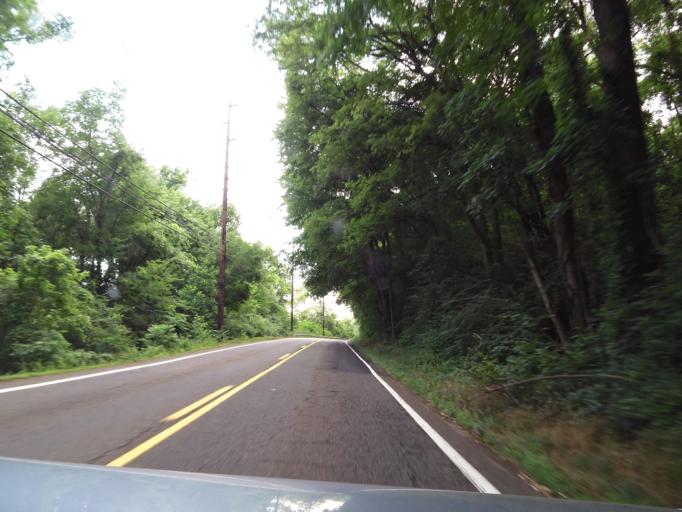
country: US
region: Tennessee
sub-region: Knox County
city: Farragut
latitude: 35.8613
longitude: -84.1306
